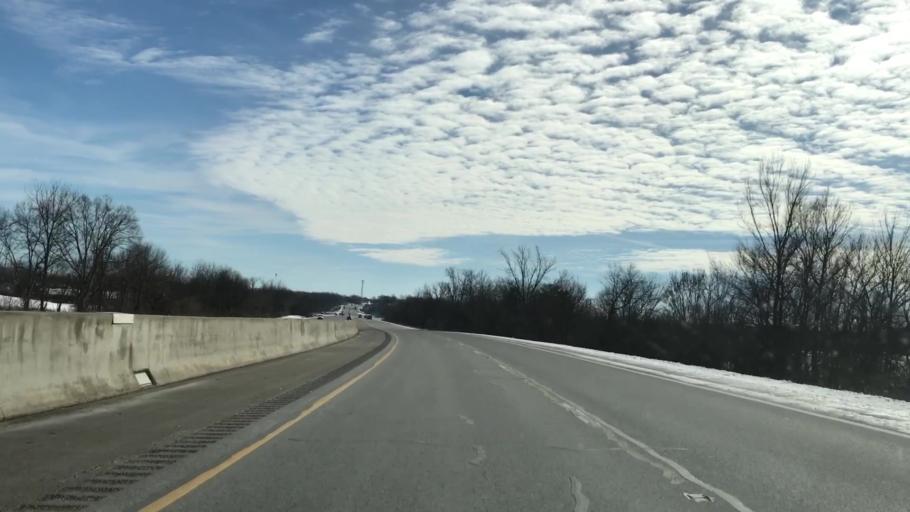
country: US
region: Kentucky
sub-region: Hardin County
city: Elizabethtown
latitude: 37.6966
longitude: -85.8791
